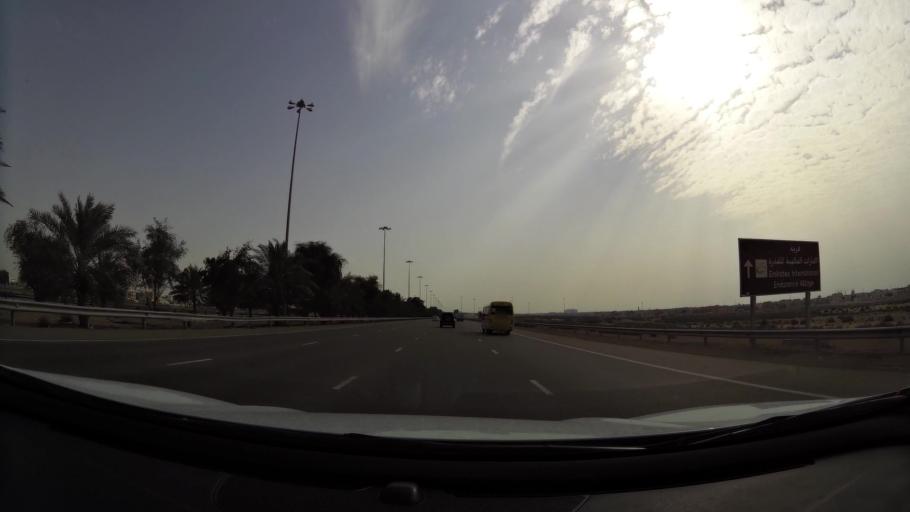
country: AE
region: Abu Dhabi
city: Abu Dhabi
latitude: 24.3760
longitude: 54.6573
